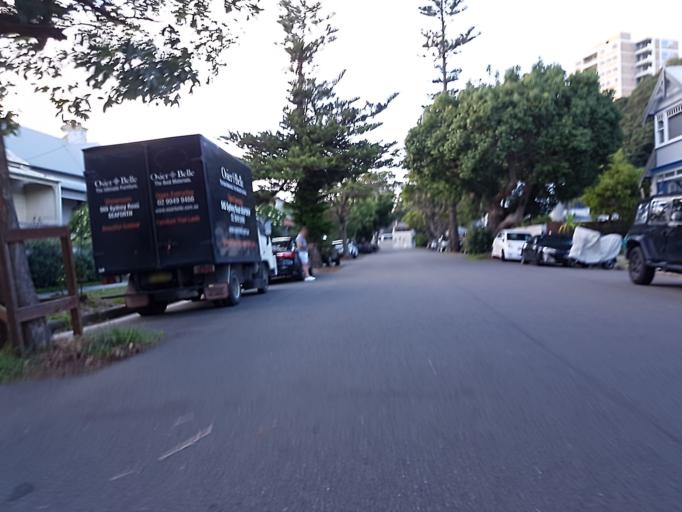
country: AU
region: New South Wales
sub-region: Manly Vale
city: Manly
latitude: -33.7912
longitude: 151.2843
